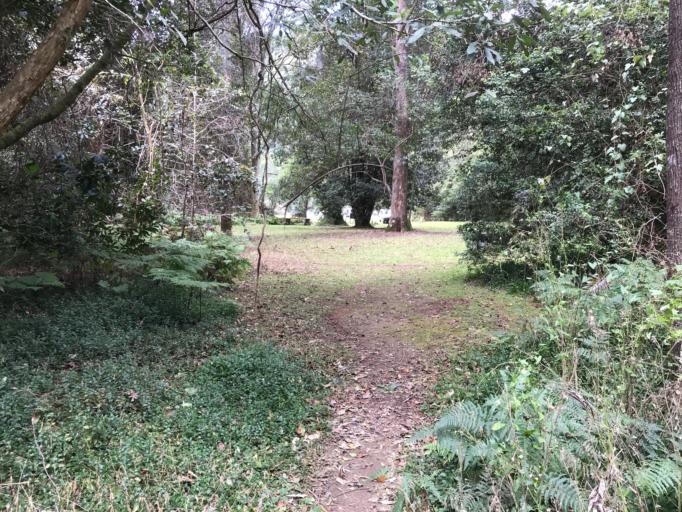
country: AU
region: New South Wales
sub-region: Dungog
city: Dungog
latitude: -32.2197
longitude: 151.7607
